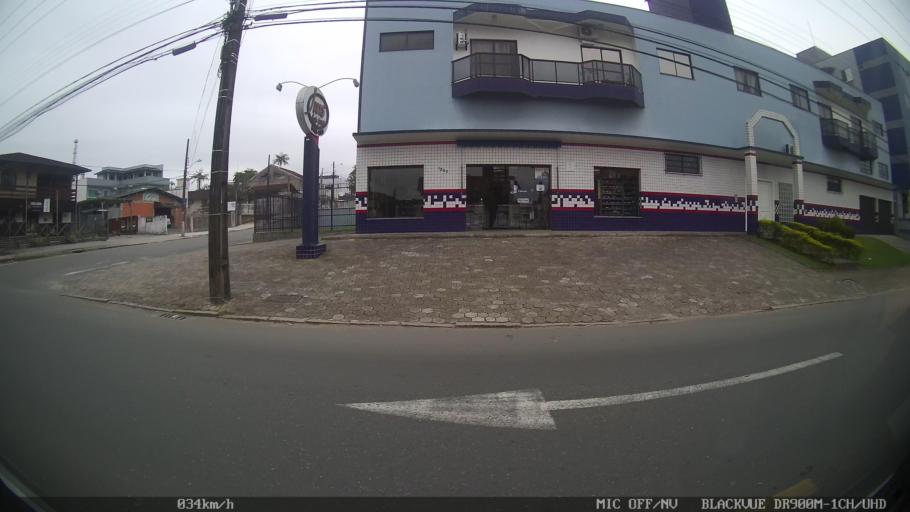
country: BR
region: Santa Catarina
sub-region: Joinville
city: Joinville
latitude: -26.2669
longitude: -48.8412
